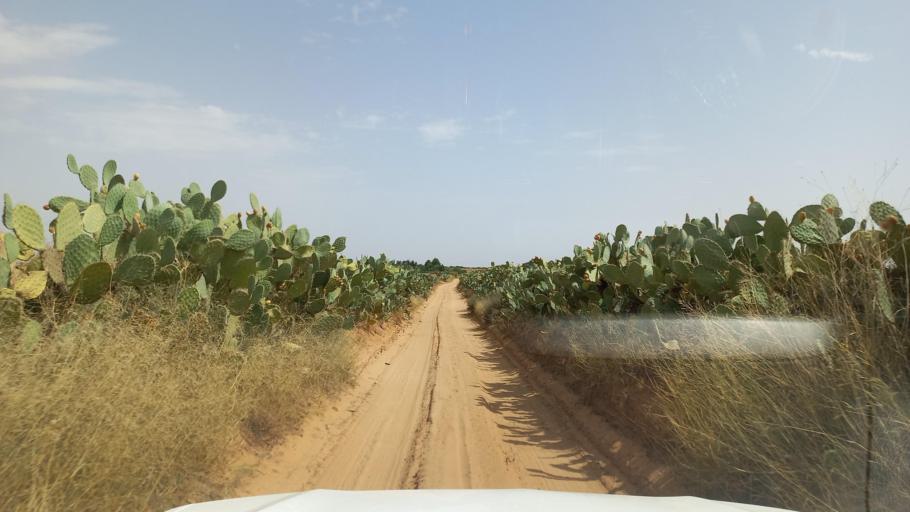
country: TN
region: Al Qasrayn
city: Kasserine
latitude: 35.2527
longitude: 9.0578
